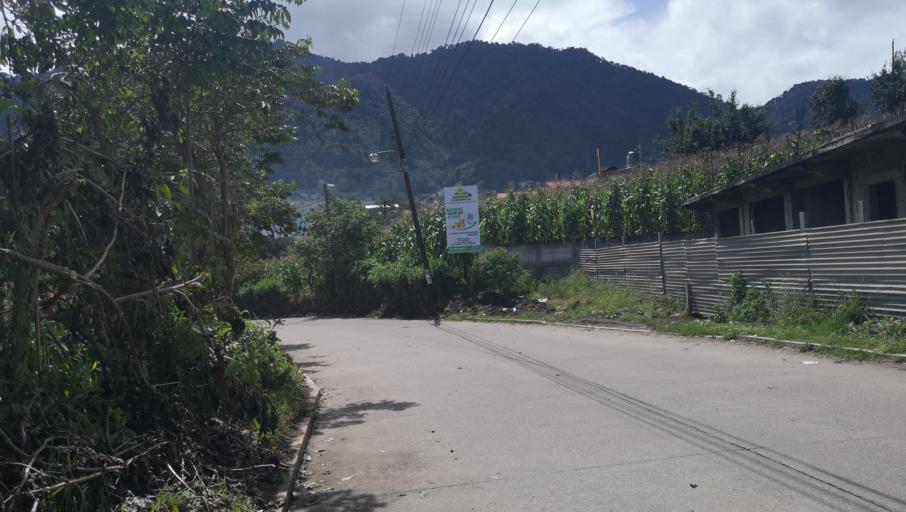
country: GT
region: Quetzaltenango
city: Cantel
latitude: 14.8159
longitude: -91.4369
